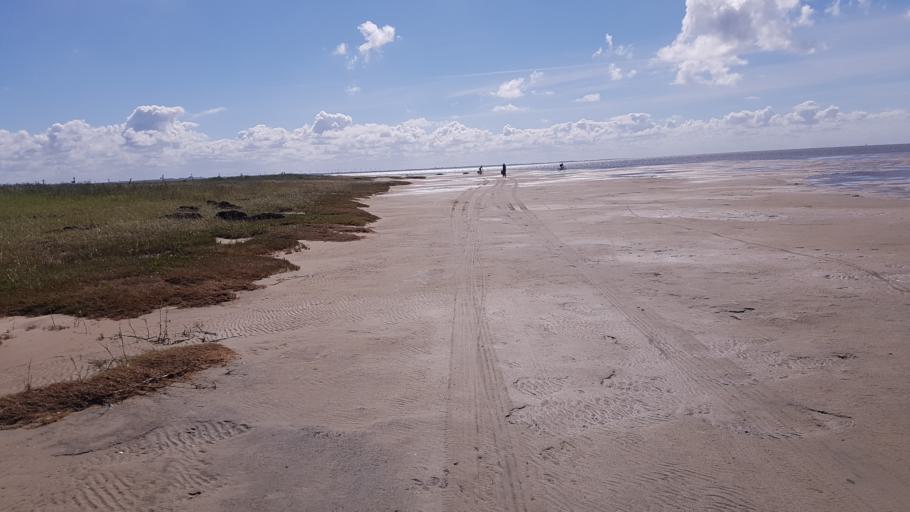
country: DE
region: Schleswig-Holstein
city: List
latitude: 55.0764
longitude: 8.5330
